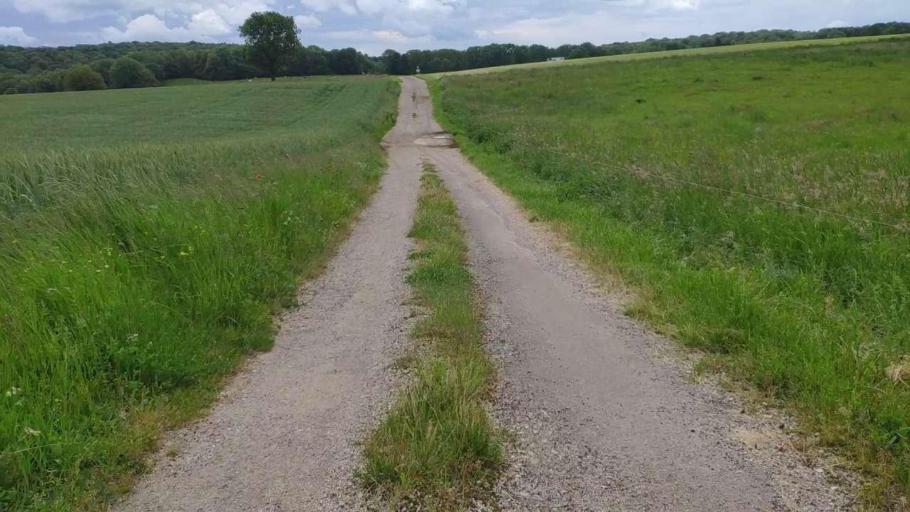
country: FR
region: Franche-Comte
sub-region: Departement du Jura
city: Poligny
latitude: 46.7613
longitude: 5.6446
